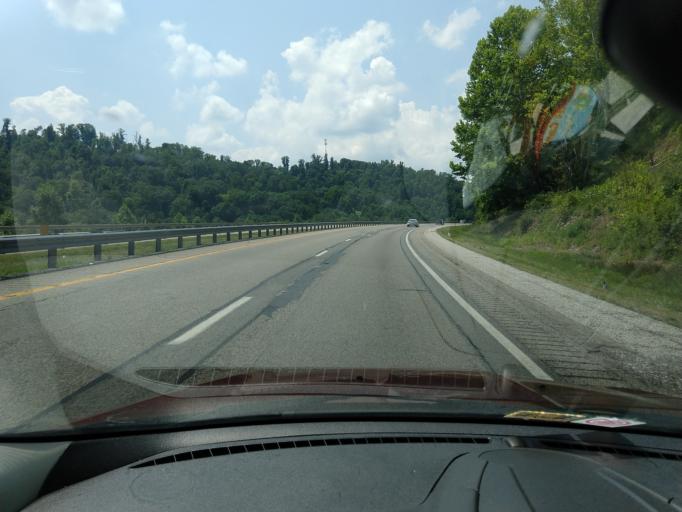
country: US
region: West Virginia
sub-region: Kanawha County
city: Charleston
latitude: 38.4234
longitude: -81.6243
